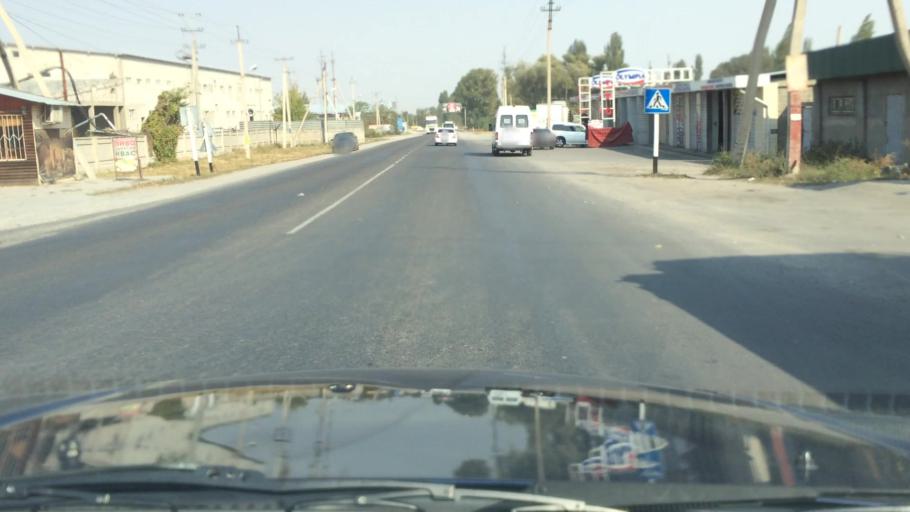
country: KG
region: Chuy
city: Lebedinovka
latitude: 42.8894
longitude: 74.6795
